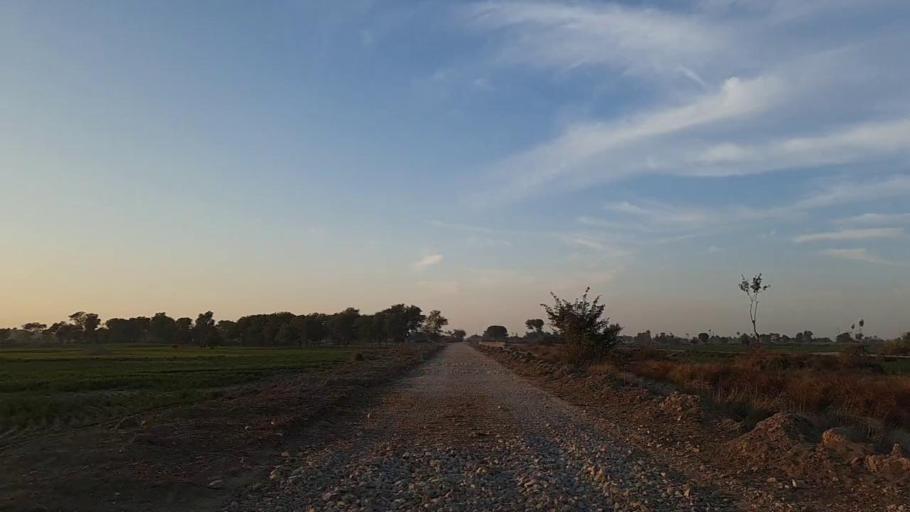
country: PK
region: Sindh
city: Bandhi
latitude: 26.6193
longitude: 68.3507
